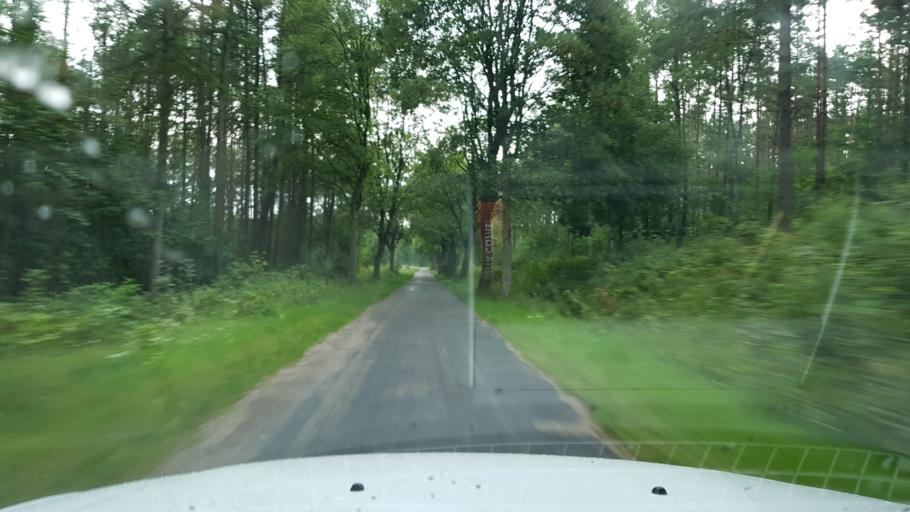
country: PL
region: West Pomeranian Voivodeship
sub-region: Powiat koszalinski
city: Bobolice
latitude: 53.8790
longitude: 16.6971
